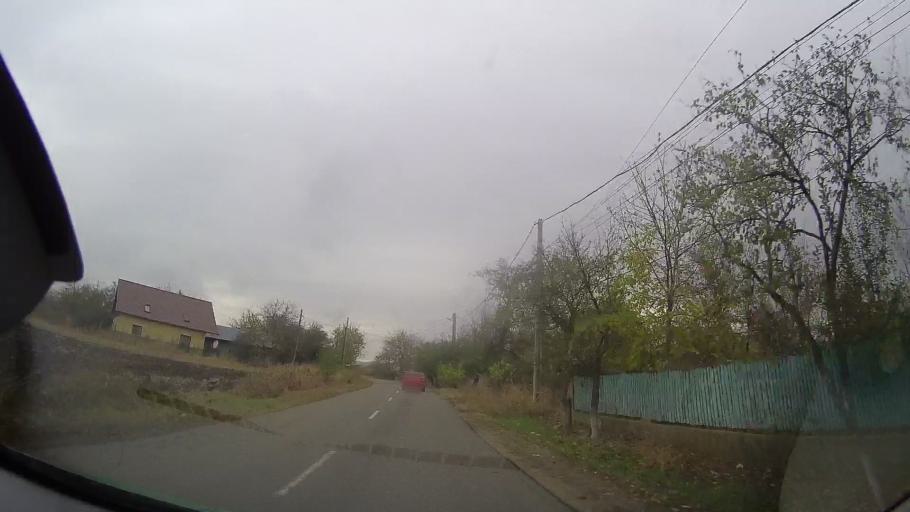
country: RO
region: Prahova
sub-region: Comuna Fantanele
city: Fantanele
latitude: 45.0152
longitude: 26.3800
